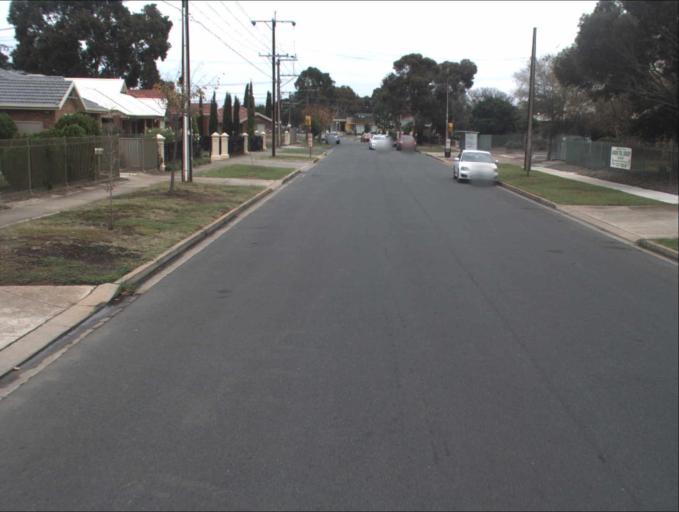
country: AU
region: South Australia
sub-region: Charles Sturt
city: Woodville North
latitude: -34.8611
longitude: 138.5567
